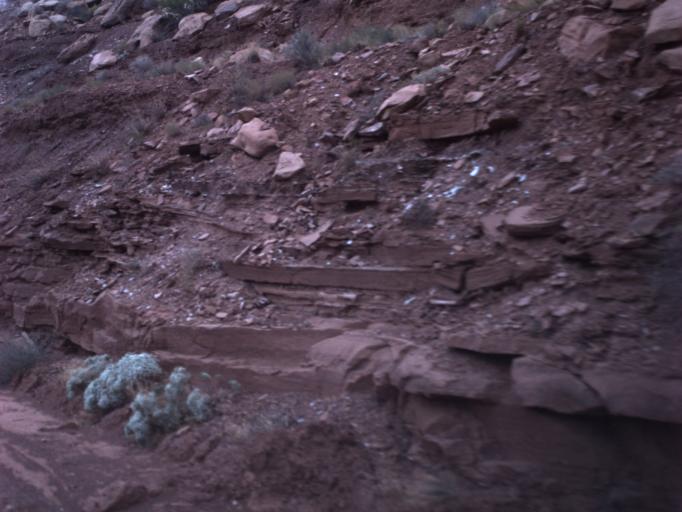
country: US
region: Utah
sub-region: Grand County
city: Moab
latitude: 38.7933
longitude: -109.3372
